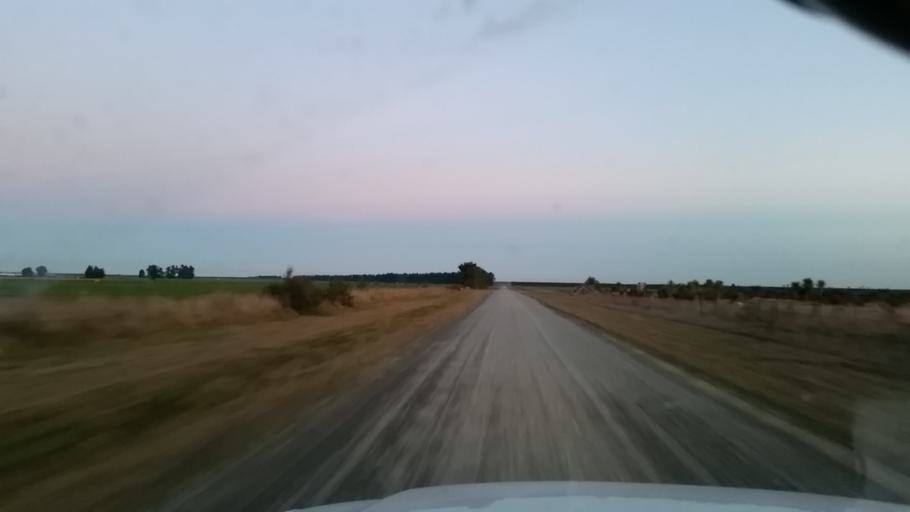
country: NZ
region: Canterbury
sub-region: Ashburton District
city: Tinwald
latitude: -43.9365
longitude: 171.6086
